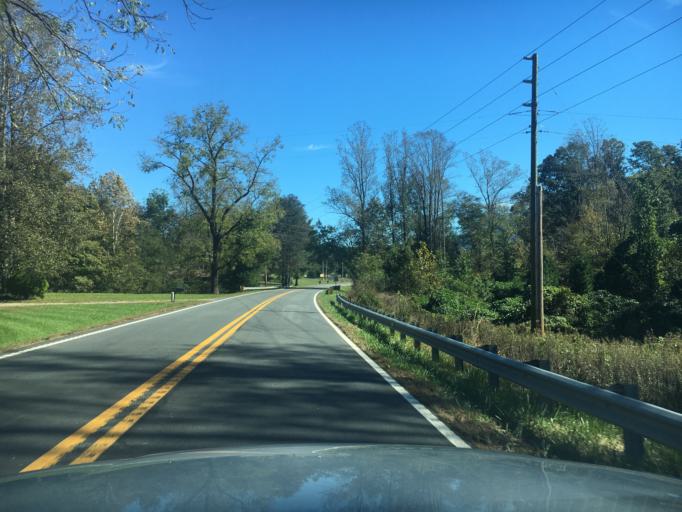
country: US
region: North Carolina
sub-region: Burke County
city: Glen Alpine
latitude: 35.6419
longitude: -81.7870
